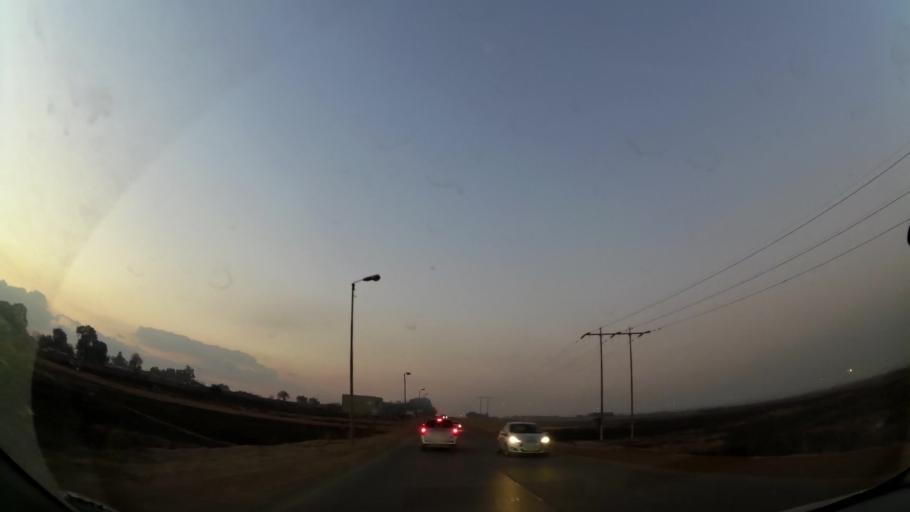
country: ZA
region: Gauteng
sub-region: Ekurhuleni Metropolitan Municipality
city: Springs
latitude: -26.3213
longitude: 28.3759
